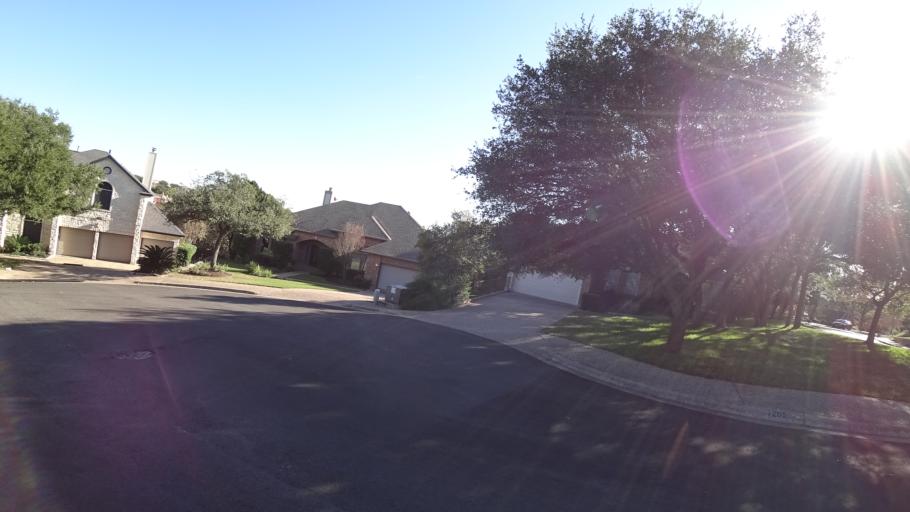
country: US
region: Texas
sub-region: Williamson County
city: Jollyville
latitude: 30.4141
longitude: -97.7748
